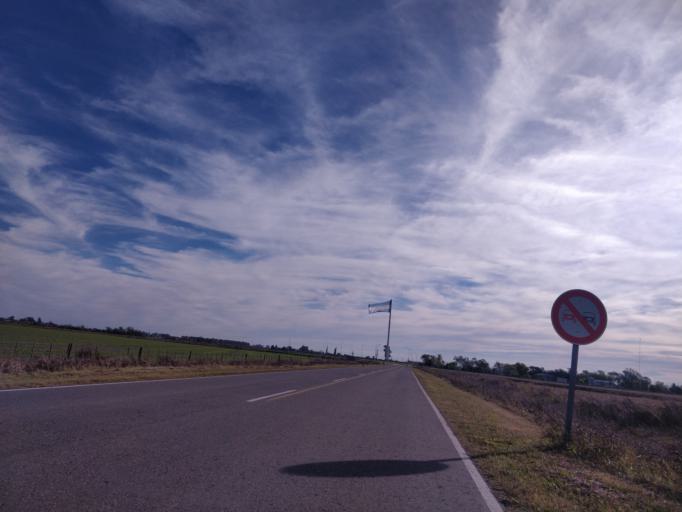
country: AR
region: Cordoba
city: Leones
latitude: -32.6428
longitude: -62.2865
